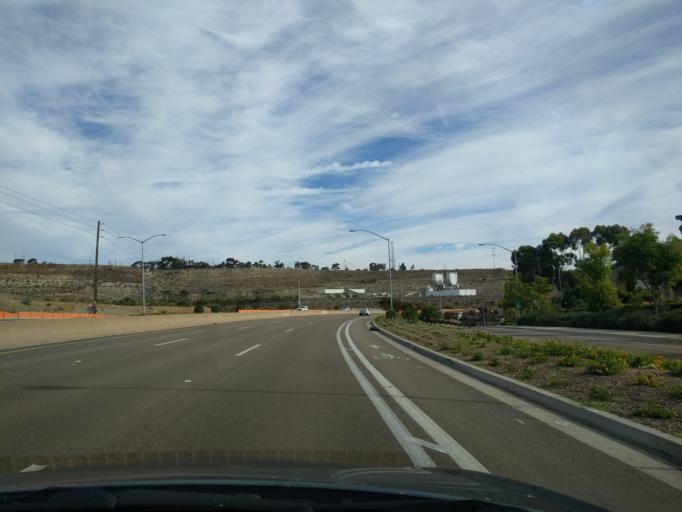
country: US
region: California
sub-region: San Diego County
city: San Diego
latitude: 32.7771
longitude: -117.1440
